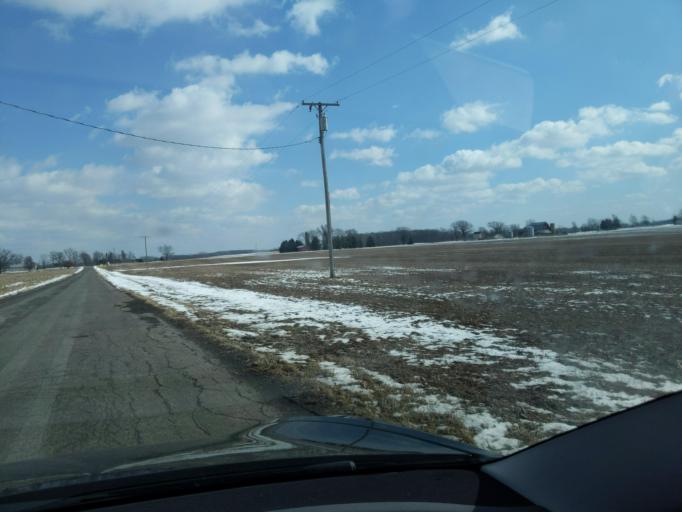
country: US
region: Michigan
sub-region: Ingham County
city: Webberville
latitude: 42.6146
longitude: -84.1754
